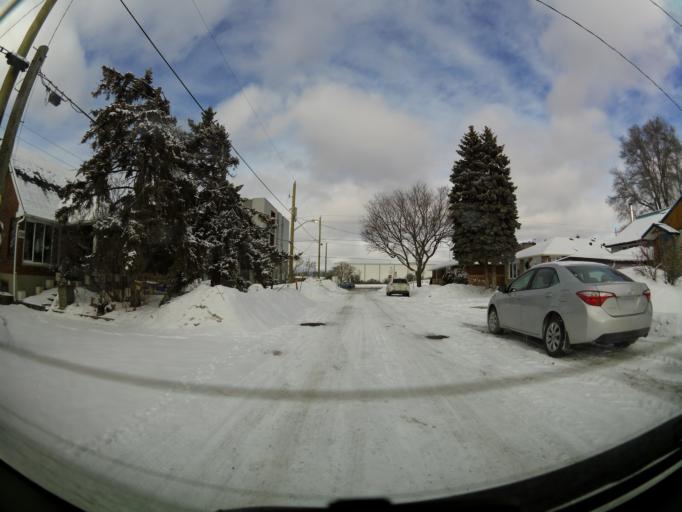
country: CA
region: Ontario
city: Ottawa
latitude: 45.4181
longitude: -75.6459
